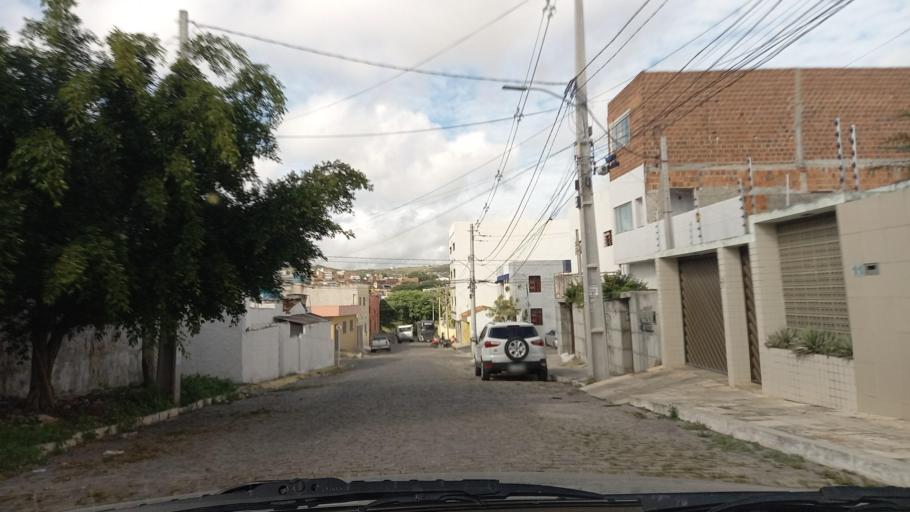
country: BR
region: Pernambuco
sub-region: Caruaru
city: Caruaru
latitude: -8.2903
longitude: -35.9820
